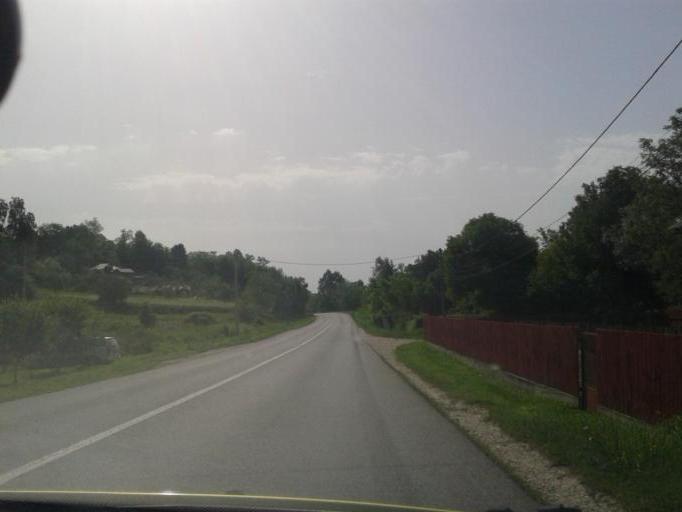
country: RO
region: Valcea
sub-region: Comuna Bunesti
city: Bunesti
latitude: 45.1125
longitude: 24.1764
